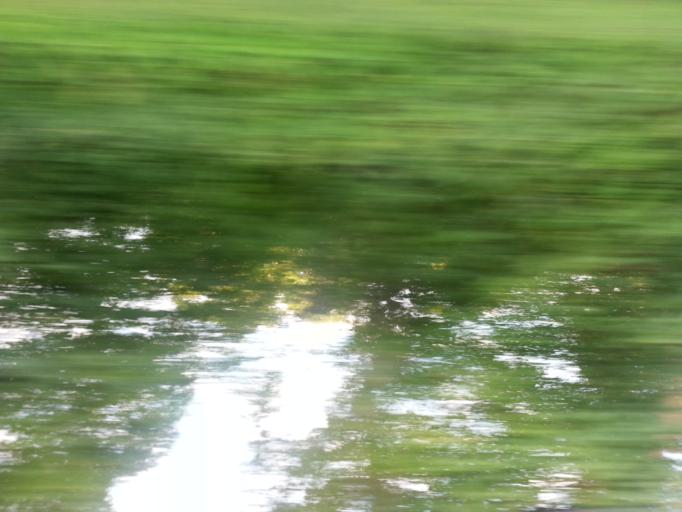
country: US
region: Tennessee
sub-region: Knox County
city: Mascot
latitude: 36.0388
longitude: -83.8164
